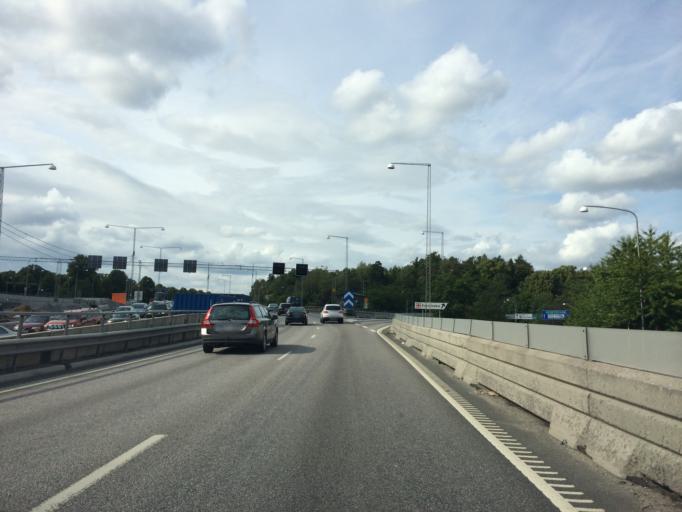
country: SE
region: Stockholm
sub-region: Norrtalje Kommun
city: Bergshamra
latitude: 59.3531
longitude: 18.0396
